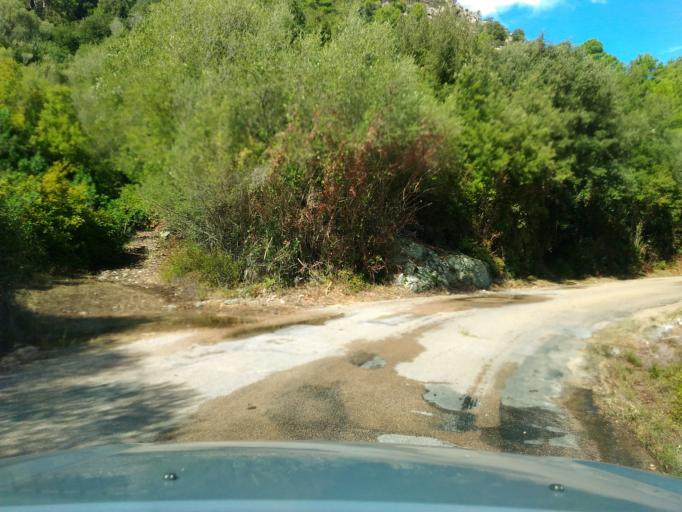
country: FR
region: Corsica
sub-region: Departement de la Corse-du-Sud
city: Porto-Vecchio
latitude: 41.7161
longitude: 9.3028
